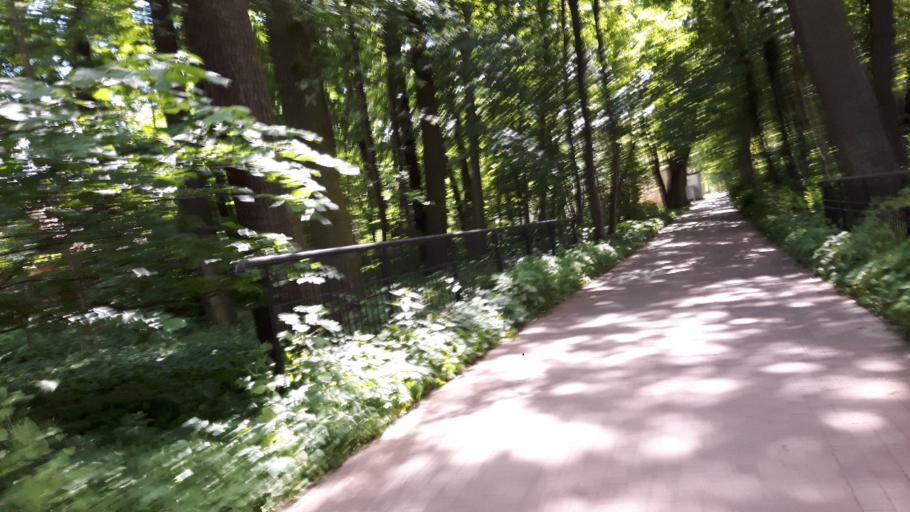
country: PL
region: Pomeranian Voivodeship
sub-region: Sopot
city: Sopot
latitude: 54.4536
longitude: 18.5633
